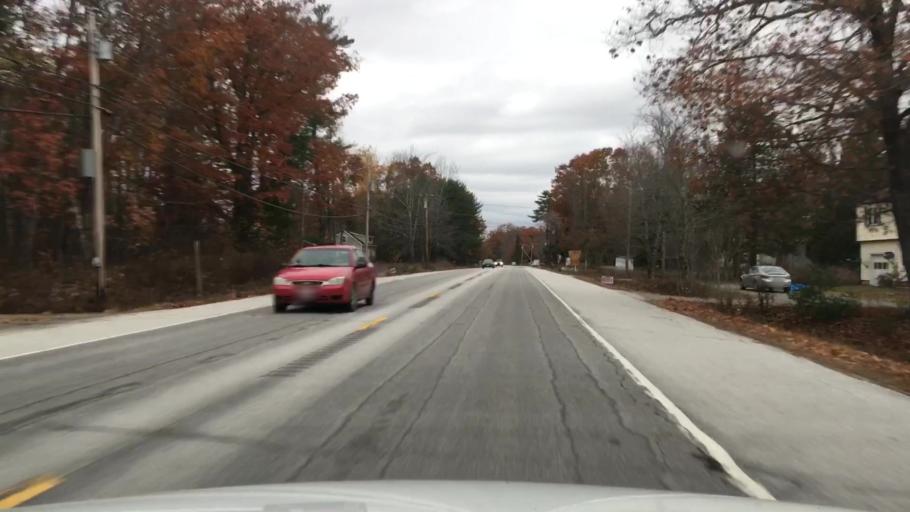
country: US
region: Maine
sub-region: Hancock County
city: Orland
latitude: 44.5635
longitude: -68.7144
